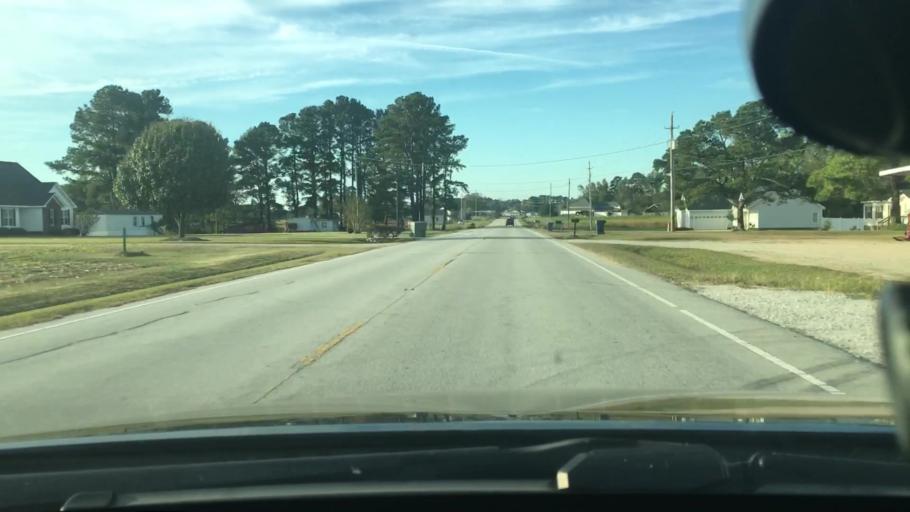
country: US
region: North Carolina
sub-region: Pitt County
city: Windsor
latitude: 35.4960
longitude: -77.3098
